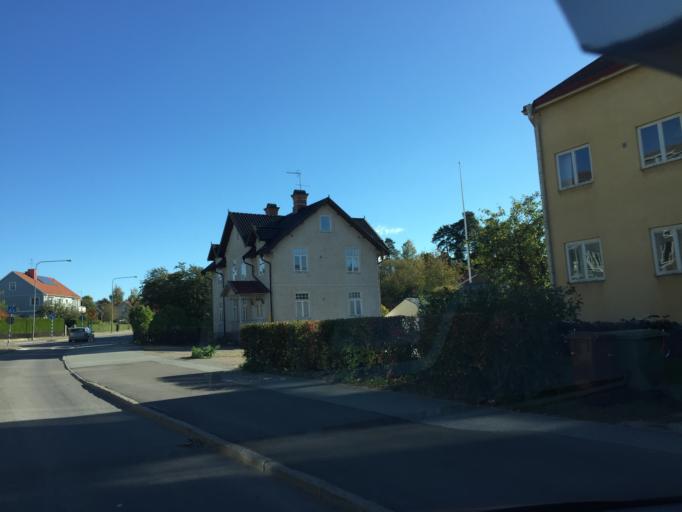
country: SE
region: OErebro
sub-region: Kumla Kommun
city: Kumla
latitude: 59.1247
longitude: 15.1444
